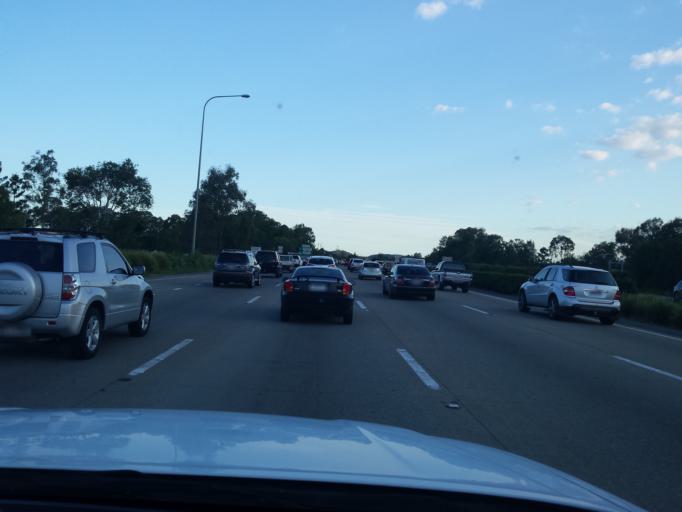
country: AU
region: Queensland
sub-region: Gold Coast
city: Oxenford
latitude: -27.8673
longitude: 153.3130
